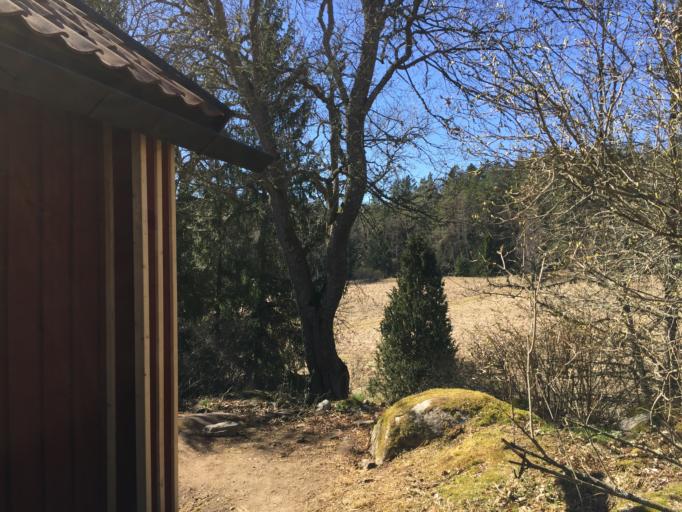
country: SE
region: Stockholm
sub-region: Salems Kommun
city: Ronninge
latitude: 59.2026
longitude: 17.7164
